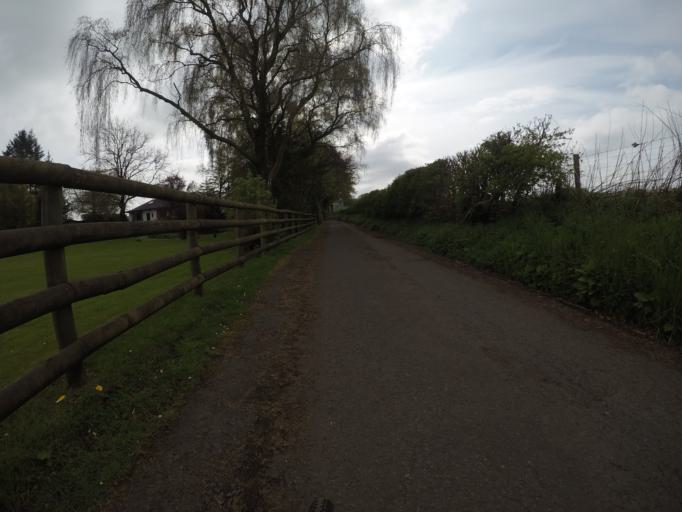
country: GB
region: Scotland
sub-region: East Renfrewshire
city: Newton Mearns
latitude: 55.7601
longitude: -4.3152
